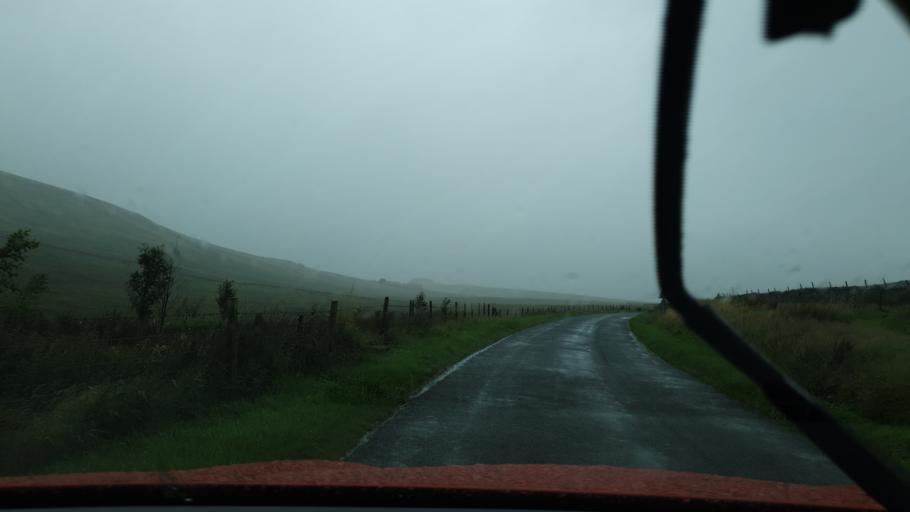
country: GB
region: England
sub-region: Cumbria
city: Millom
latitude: 54.3466
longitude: -3.2499
